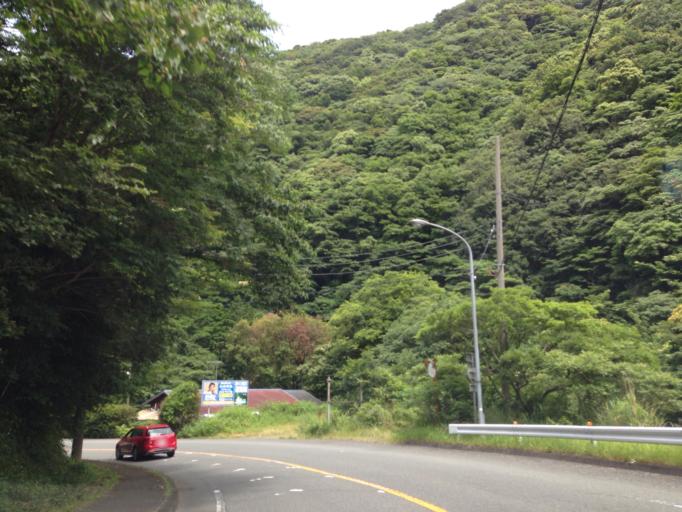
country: JP
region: Shizuoka
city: Heda
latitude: 34.9055
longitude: 138.8117
